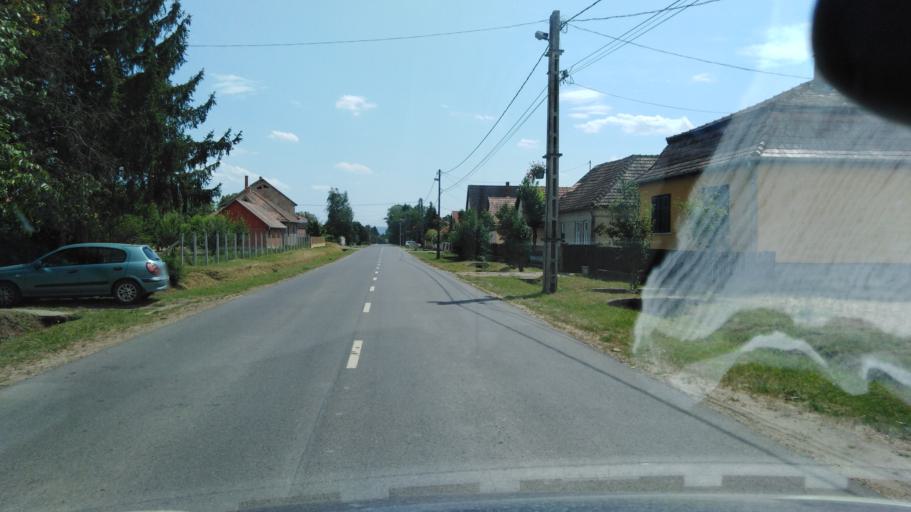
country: HU
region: Nograd
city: Szecseny
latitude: 48.1465
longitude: 19.5316
